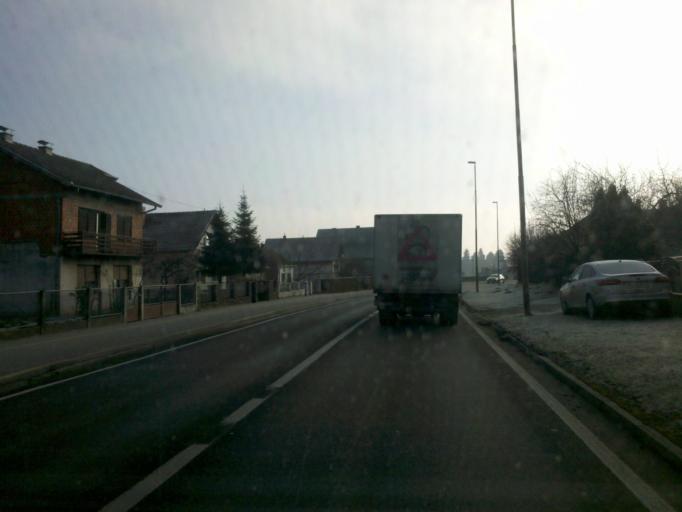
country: HR
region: Koprivnicko-Krizevacka
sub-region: Grad Koprivnica
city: Koprivnica
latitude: 46.1740
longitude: 16.8099
